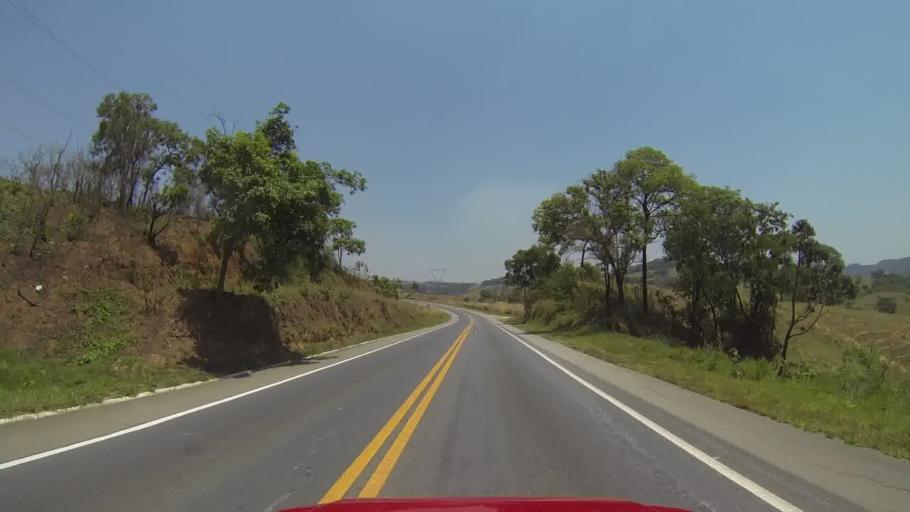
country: BR
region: Minas Gerais
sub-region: Itapecerica
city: Itapecerica
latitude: -20.3283
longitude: -45.2254
